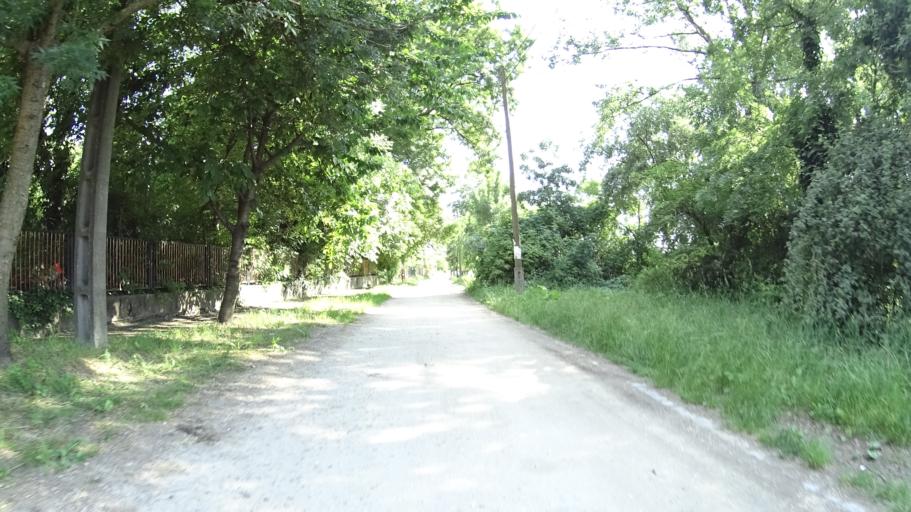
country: HU
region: Budapest
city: Budapest XXIII. keruelet
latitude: 47.3829
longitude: 19.1025
